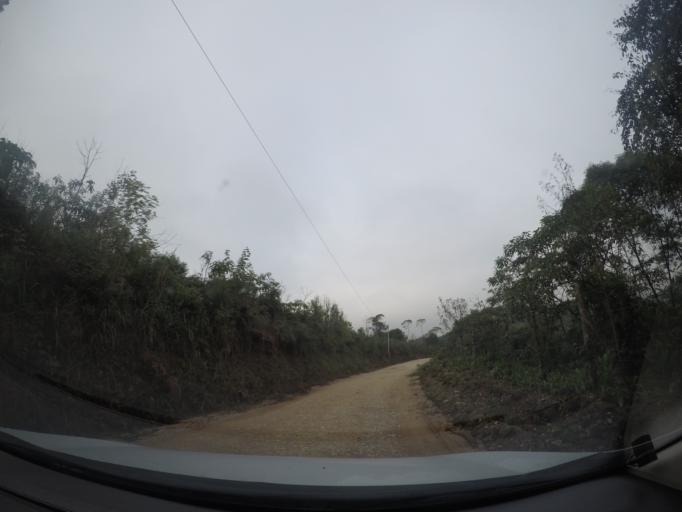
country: BR
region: Parana
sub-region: Colombo
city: Colombo
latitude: -25.3126
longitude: -49.2454
